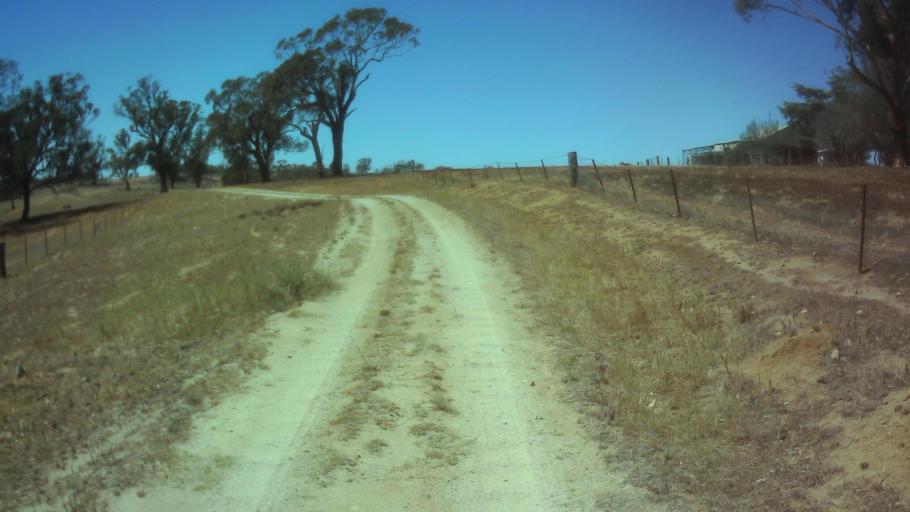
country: AU
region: New South Wales
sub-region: Cowra
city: Cowra
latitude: -33.8894
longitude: 148.4987
